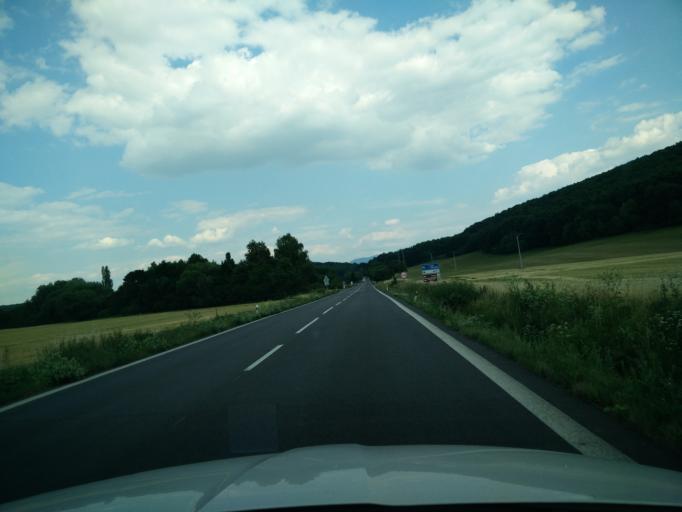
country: SK
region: Nitriansky
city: Novaky
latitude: 48.7221
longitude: 18.4922
